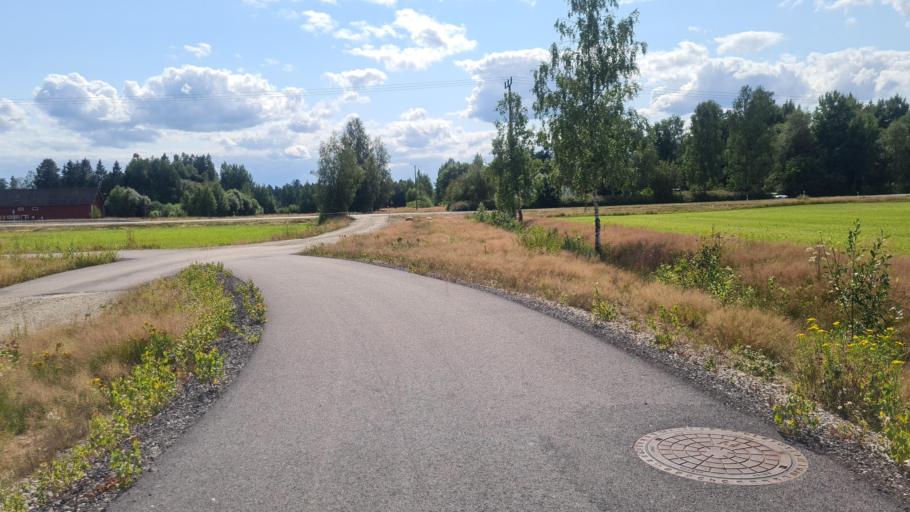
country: SE
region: Kronoberg
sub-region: Ljungby Kommun
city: Ljungby
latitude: 56.8522
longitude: 13.9700
